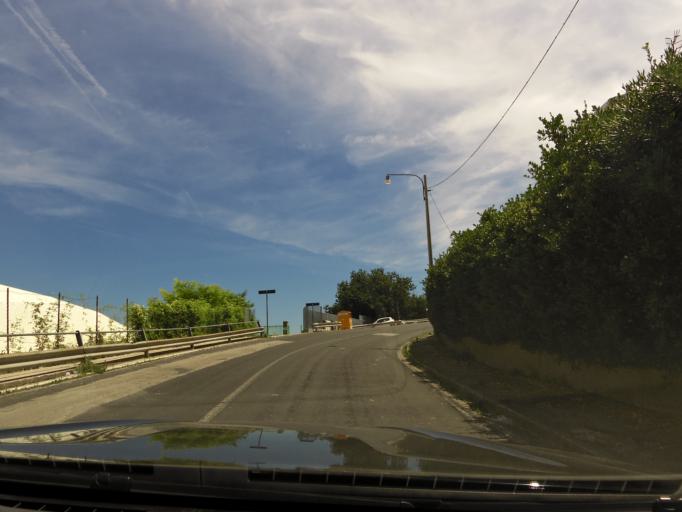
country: IT
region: The Marches
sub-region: Provincia di Ancona
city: Pietra la Croce
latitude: 43.6117
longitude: 13.5322
